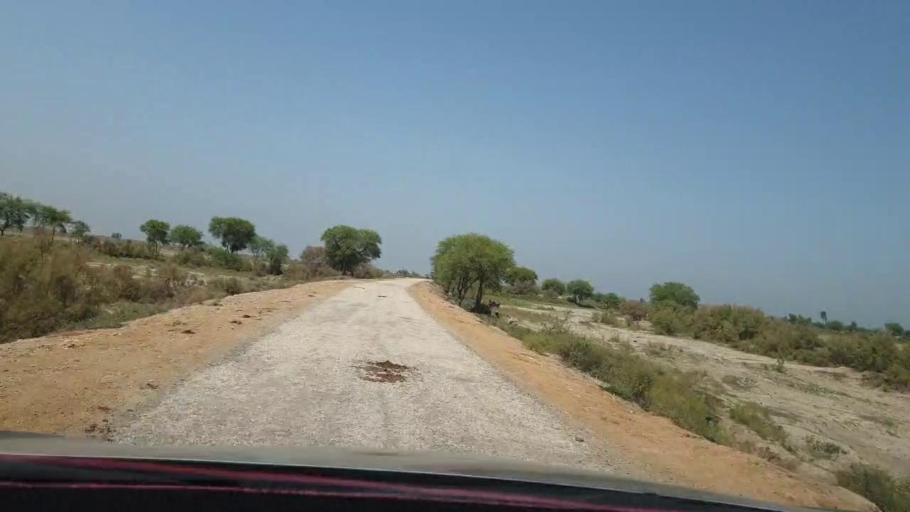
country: PK
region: Sindh
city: Warah
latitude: 27.5094
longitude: 67.7046
